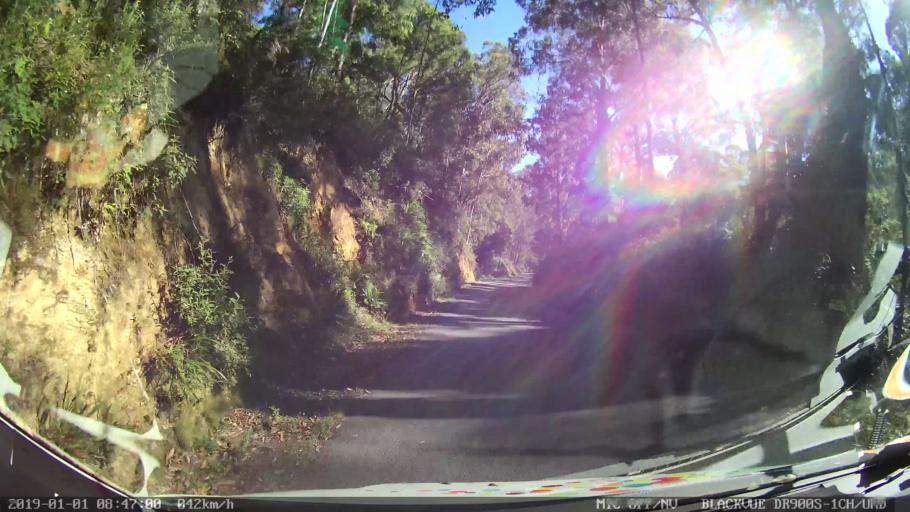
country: AU
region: New South Wales
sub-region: Snowy River
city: Jindabyne
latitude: -36.2968
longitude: 148.1954
